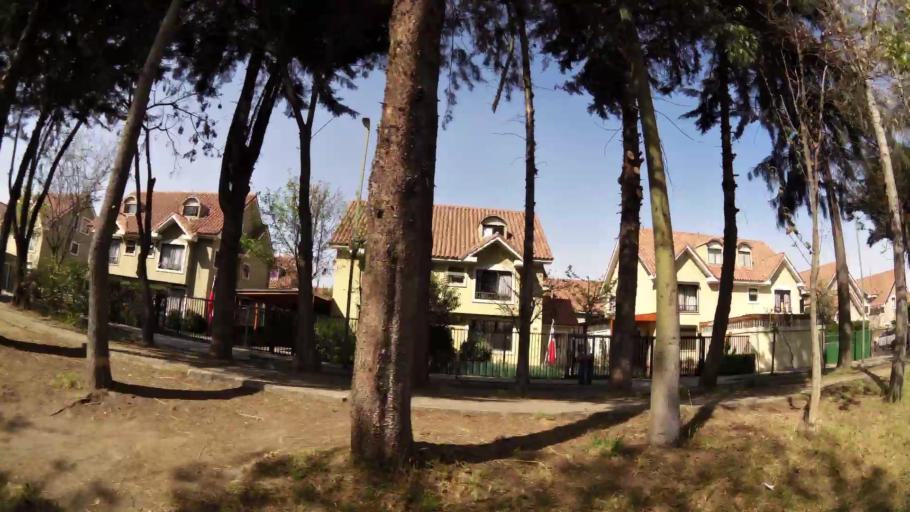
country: CL
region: Santiago Metropolitan
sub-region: Provincia de Santiago
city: Villa Presidente Frei, Nunoa, Santiago, Chile
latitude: -33.5318
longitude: -70.5700
